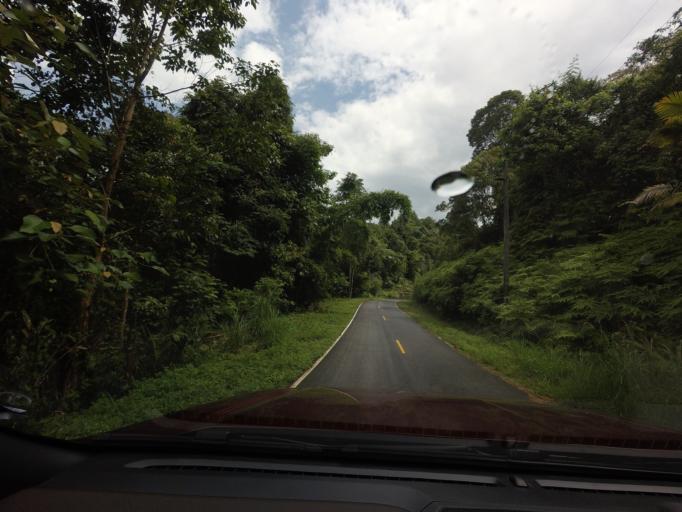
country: TH
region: Narathiwat
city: Sukhirin
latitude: 5.9260
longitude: 101.6472
